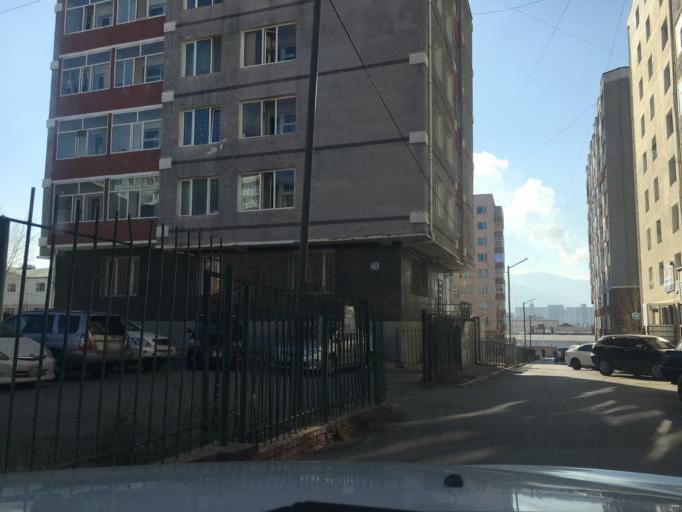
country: MN
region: Ulaanbaatar
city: Ulaanbaatar
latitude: 47.9197
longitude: 106.8680
